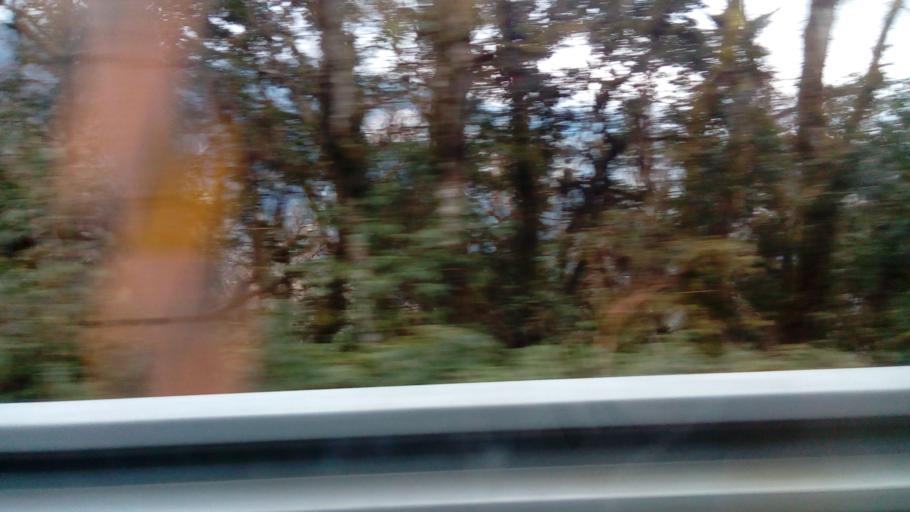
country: TW
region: Taiwan
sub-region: Hualien
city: Hualian
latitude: 24.3988
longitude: 121.3672
